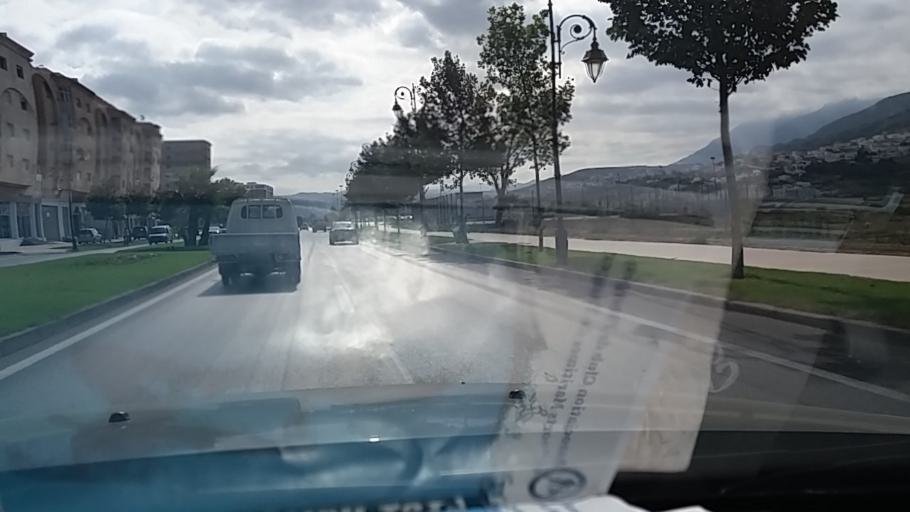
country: MA
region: Tanger-Tetouan
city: Tetouan
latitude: 35.5633
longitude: -5.3766
